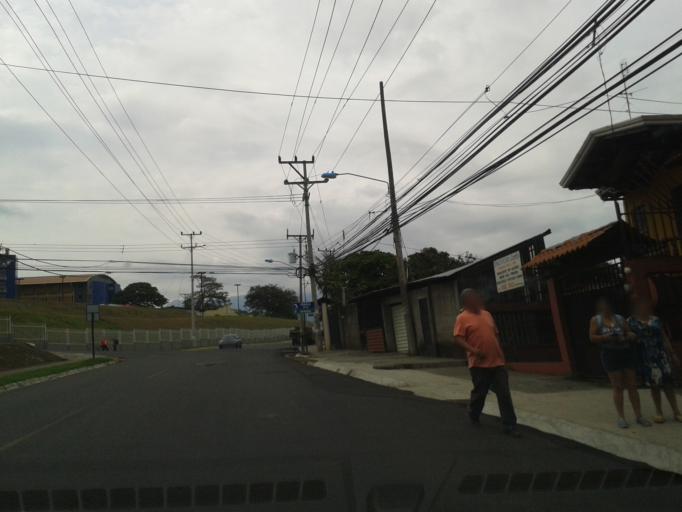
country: CR
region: Heredia
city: San Francisco
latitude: 9.9879
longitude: -84.1208
